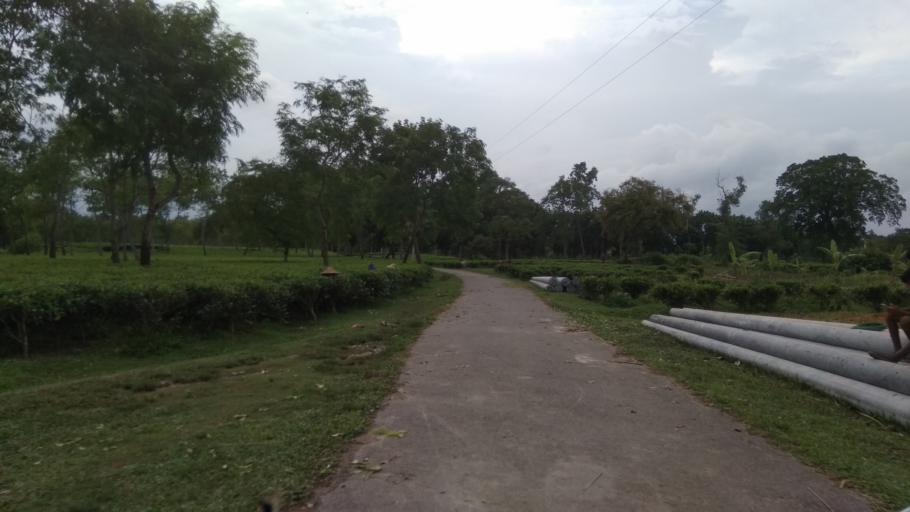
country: IN
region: Tripura
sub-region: Dhalai
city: Kamalpur
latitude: 24.1761
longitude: 91.8794
